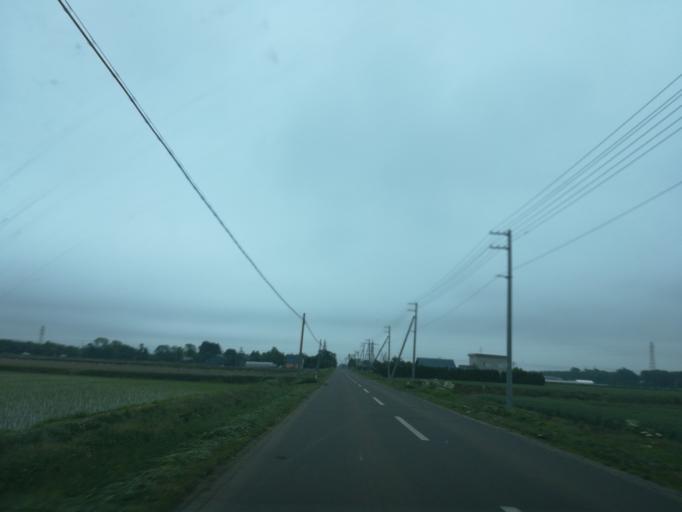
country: JP
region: Hokkaido
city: Ebetsu
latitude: 43.0591
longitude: 141.6205
